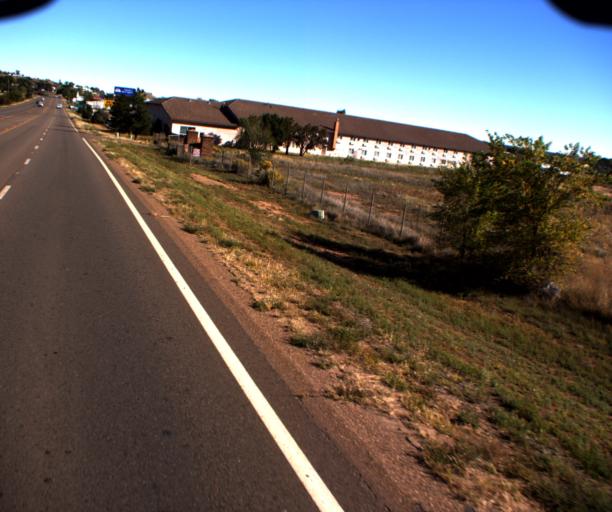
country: US
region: Arizona
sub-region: Navajo County
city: Taylor
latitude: 34.4798
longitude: -110.0844
